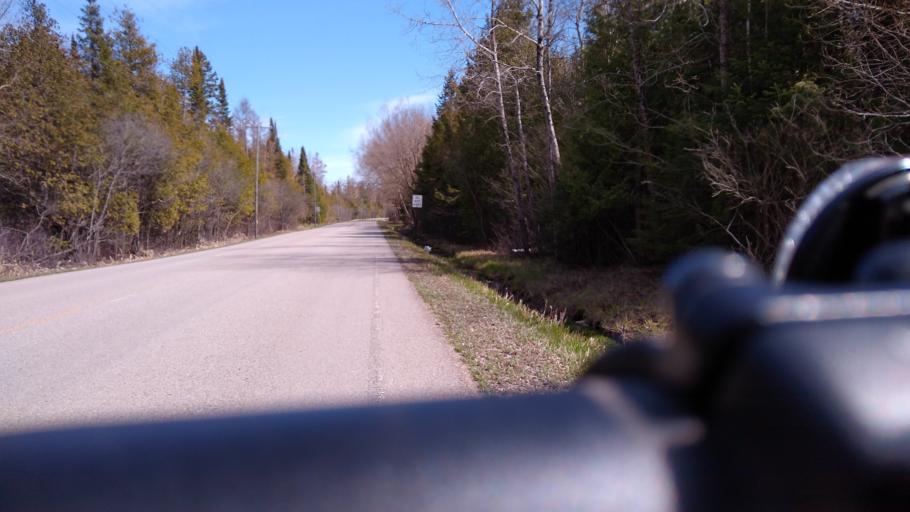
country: US
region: Michigan
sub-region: Delta County
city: Escanaba
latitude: 45.6854
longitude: -87.1500
